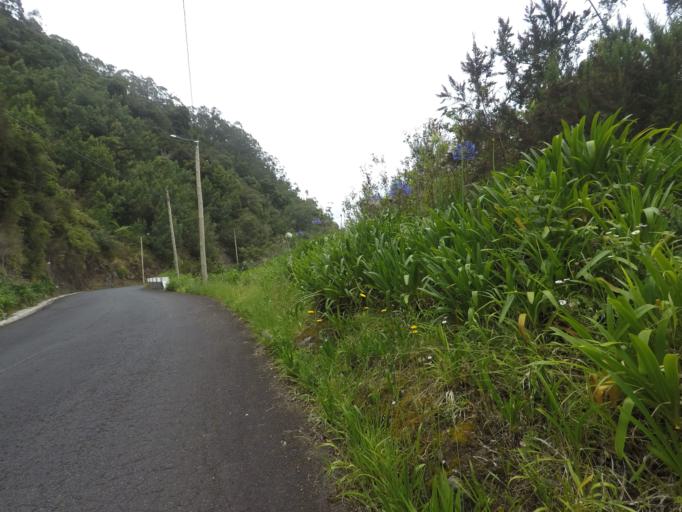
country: PT
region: Madeira
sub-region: Santana
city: Santana
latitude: 32.7918
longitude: -16.8631
